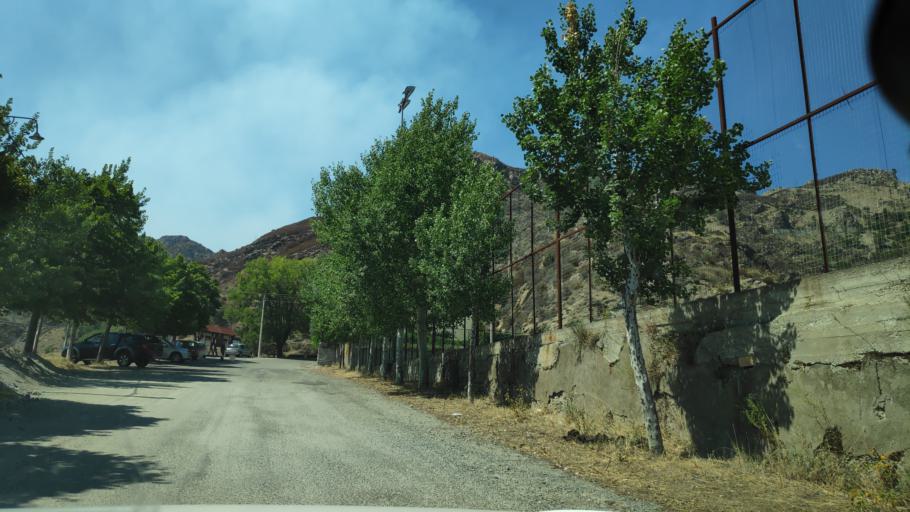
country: IT
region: Calabria
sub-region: Provincia di Reggio Calabria
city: Bova
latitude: 37.9985
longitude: 15.9311
